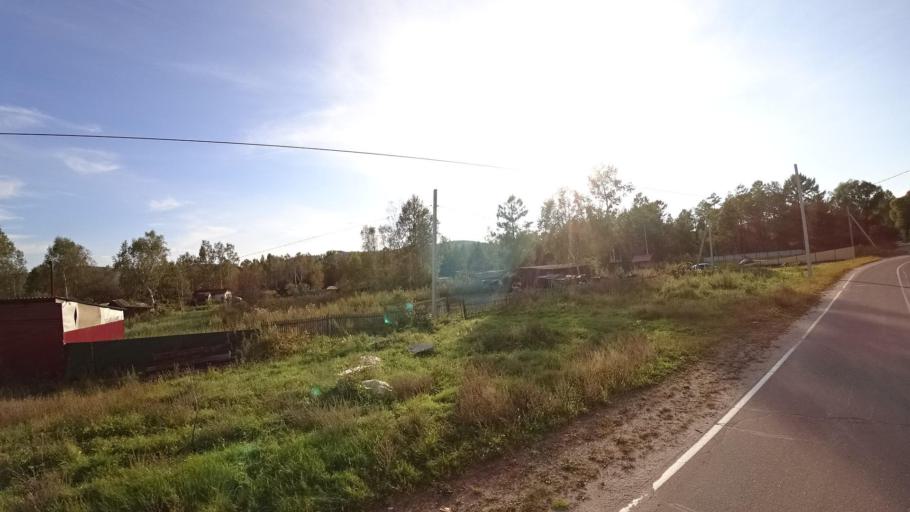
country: RU
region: Jewish Autonomous Oblast
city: Kul'dur
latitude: 49.2032
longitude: 131.6211
